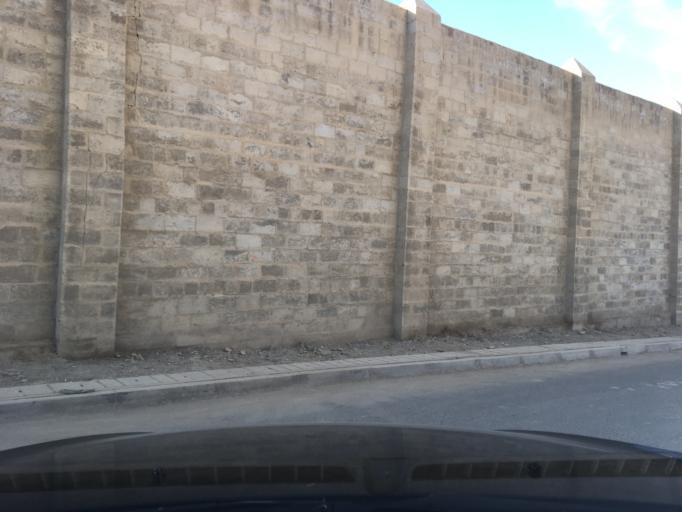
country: MN
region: Ulaanbaatar
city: Ulaanbaatar
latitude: 47.8757
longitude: 106.9144
